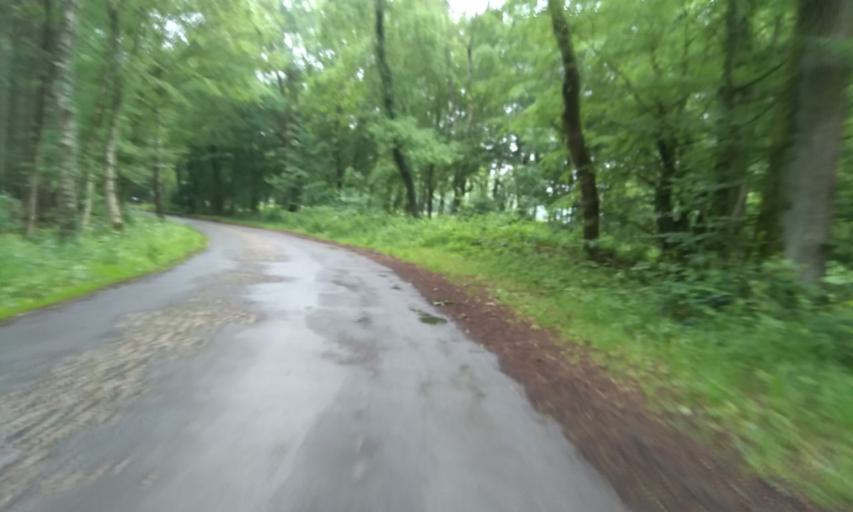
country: DE
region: Lower Saxony
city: Deinste
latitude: 53.5335
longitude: 9.4347
